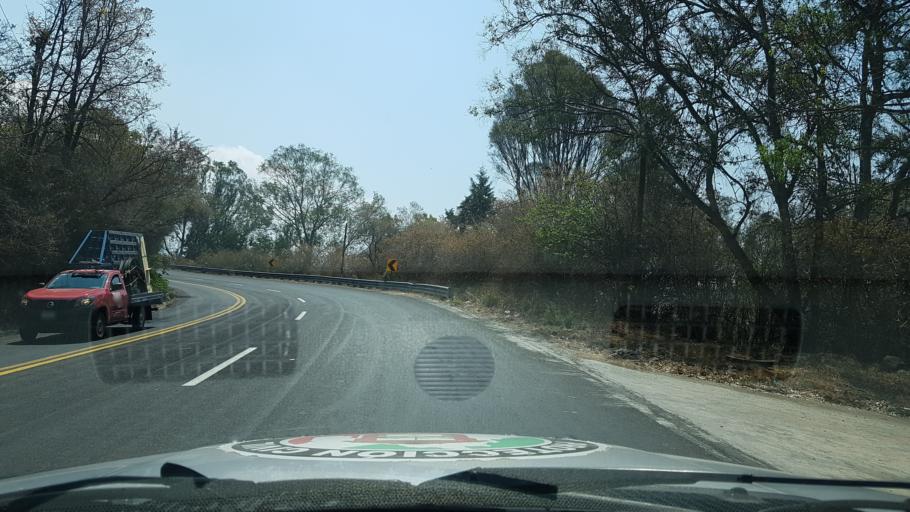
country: MX
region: Mexico
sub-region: Tepetlixpa
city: Nepantla de Sor Juana Ines de la Cruz
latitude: 18.9892
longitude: -98.8297
